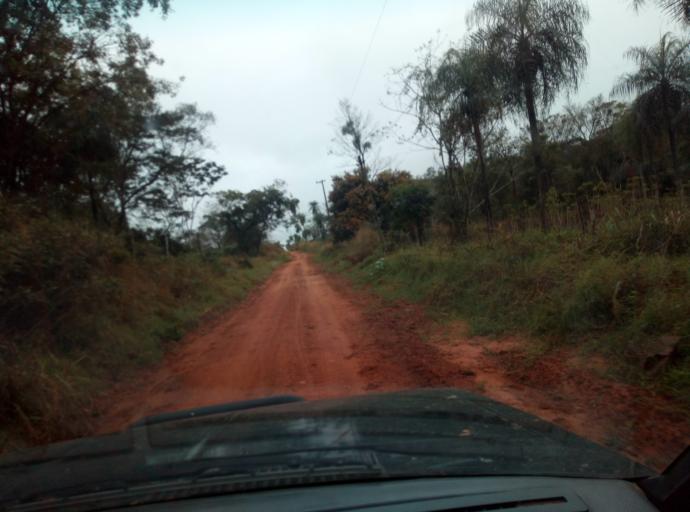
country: PY
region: Caaguazu
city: Carayao
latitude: -25.1904
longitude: -56.3626
